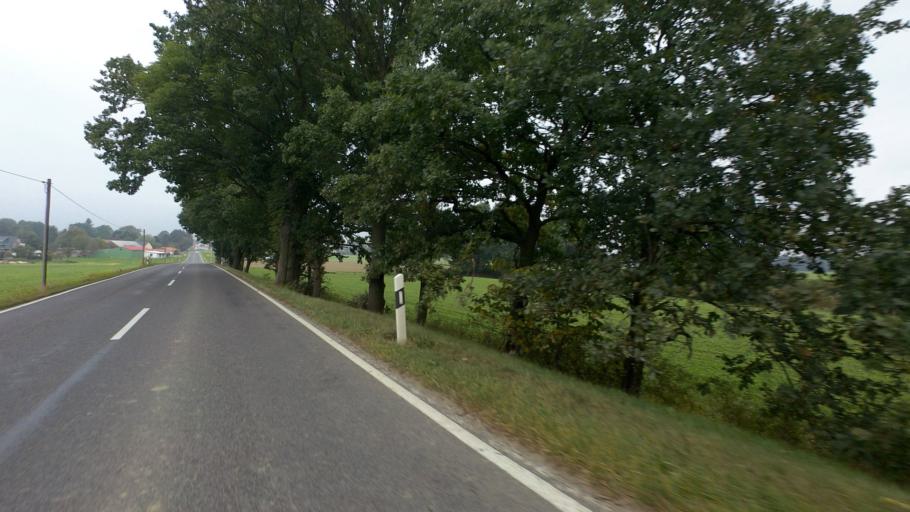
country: DE
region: Saxony
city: Arnsdorf
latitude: 51.0837
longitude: 14.0241
